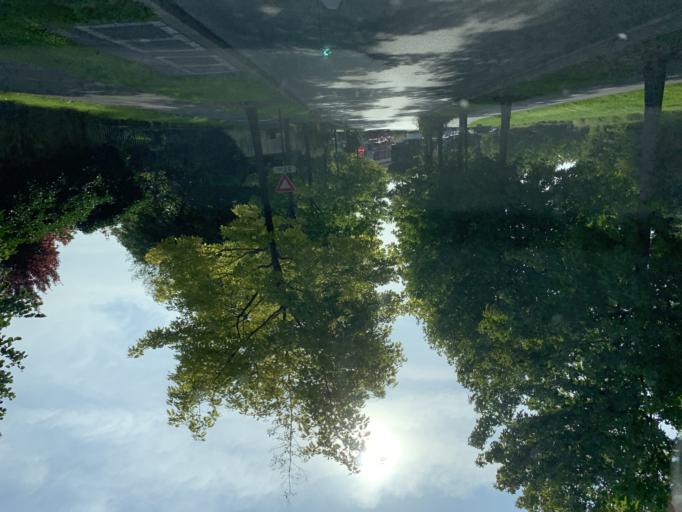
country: FR
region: Ile-de-France
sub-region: Departement de Seine-et-Marne
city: Claye-Souilly
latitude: 48.9447
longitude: 2.6951
